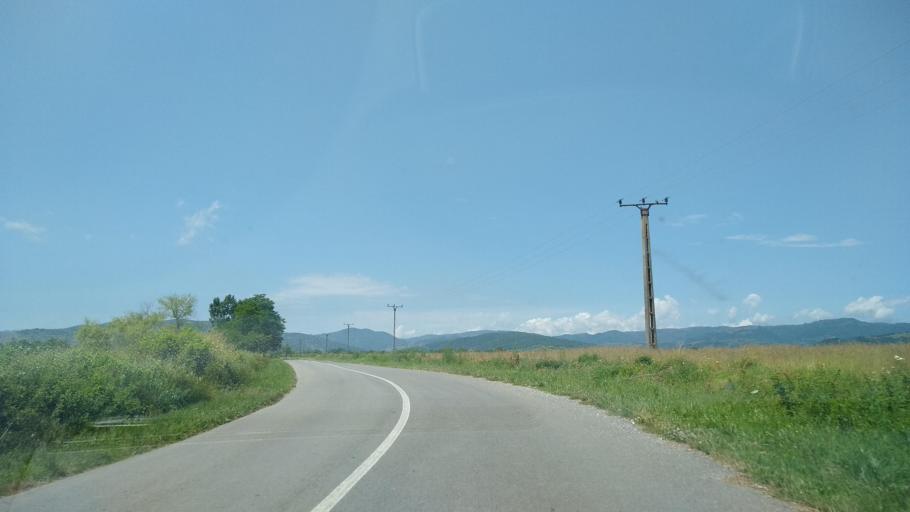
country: RO
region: Hunedoara
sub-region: Comuna Totesti
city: Totesti
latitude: 45.5775
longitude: 22.8522
